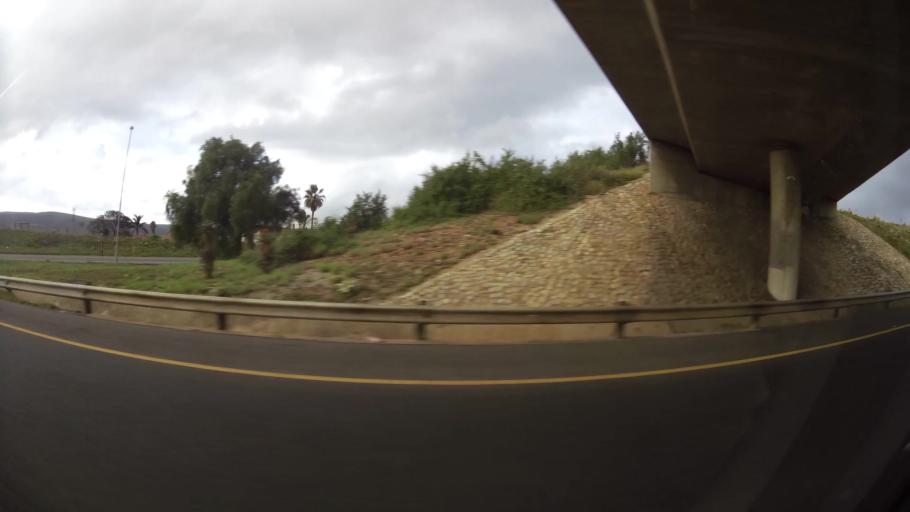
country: ZA
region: Eastern Cape
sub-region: Nelson Mandela Bay Metropolitan Municipality
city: Uitenhage
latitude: -33.8103
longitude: 25.4955
